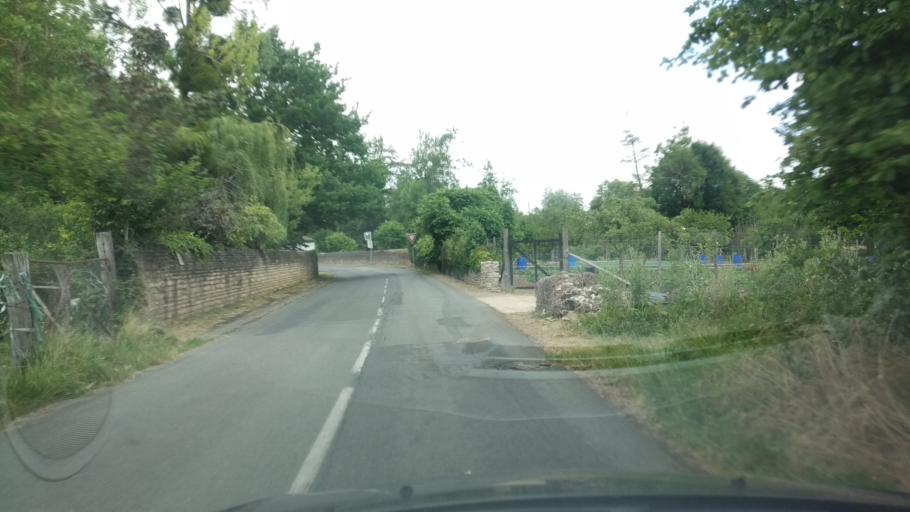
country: FR
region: Poitou-Charentes
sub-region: Departement de la Vienne
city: Vouille
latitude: 46.6359
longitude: 0.1683
